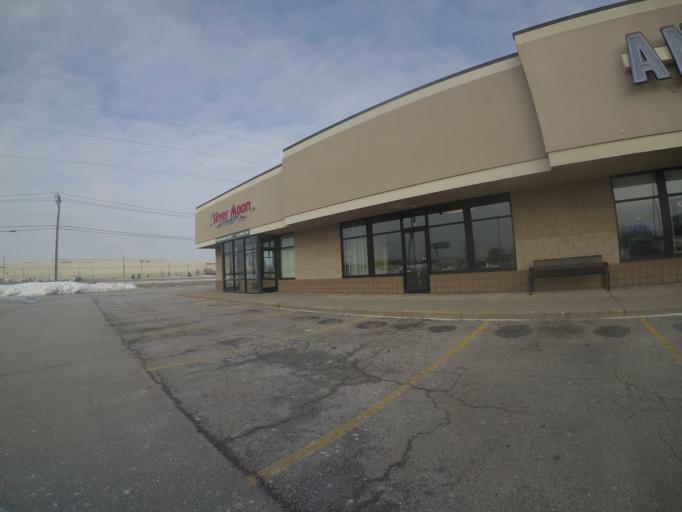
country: US
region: Ohio
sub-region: Wood County
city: Rossford
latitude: 41.5630
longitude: -83.5443
